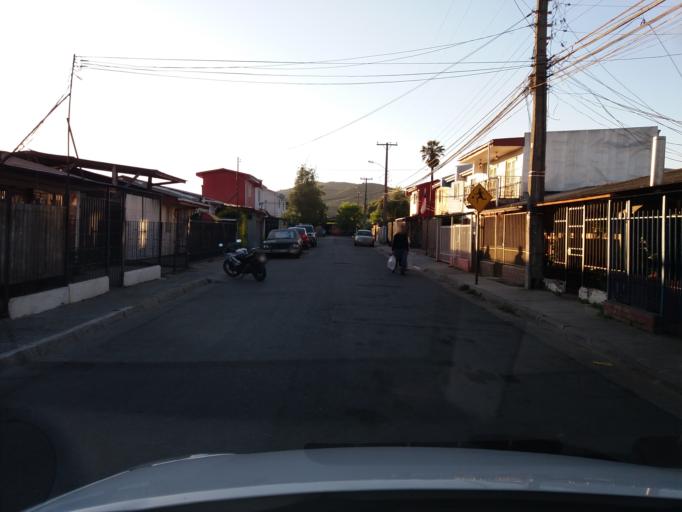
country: CL
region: Valparaiso
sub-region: Provincia de Quillota
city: Quillota
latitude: -32.8939
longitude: -71.2627
